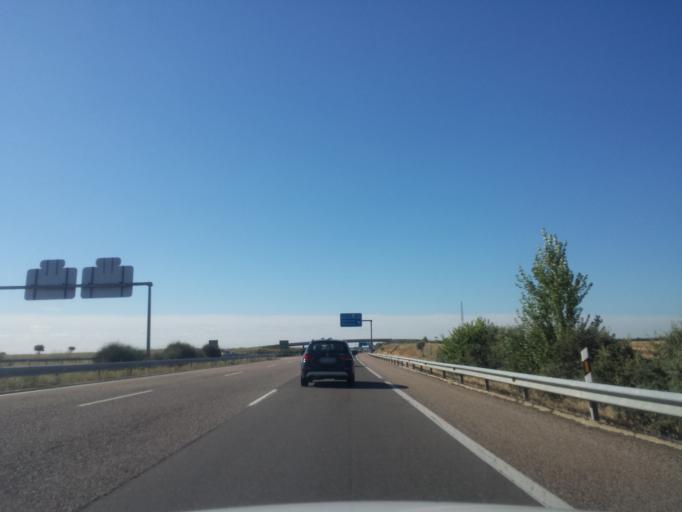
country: ES
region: Castille and Leon
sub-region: Provincia de Zamora
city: San Cristobal de Entrevinas
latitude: 42.0447
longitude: -5.6739
